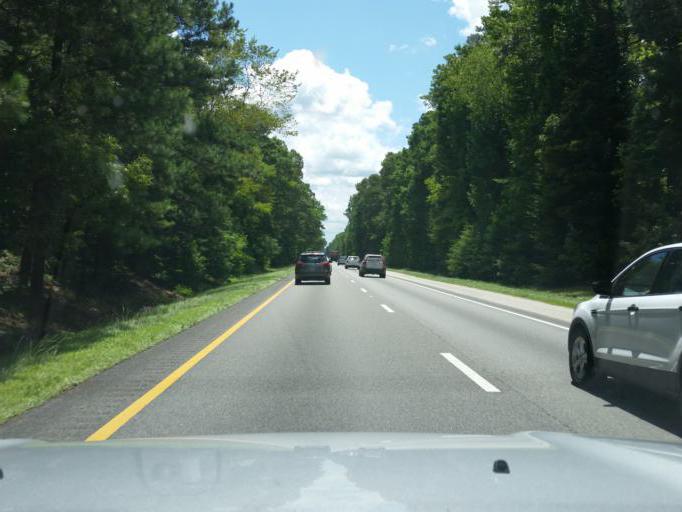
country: US
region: Virginia
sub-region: City of Williamsburg
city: Williamsburg
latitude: 37.3390
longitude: -76.7163
